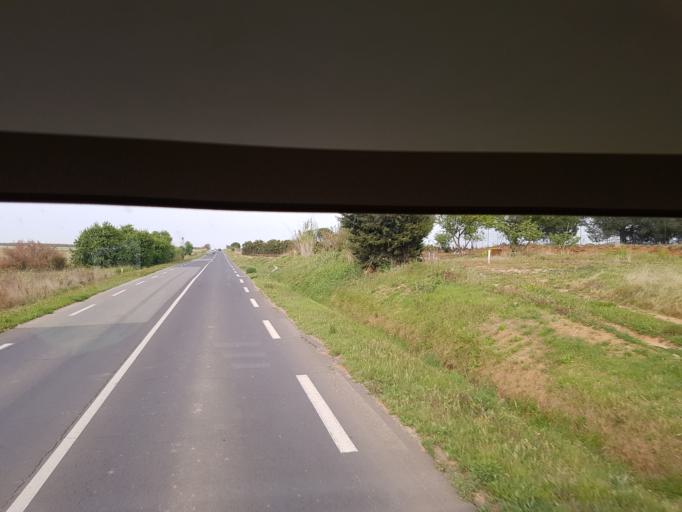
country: FR
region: Languedoc-Roussillon
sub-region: Departement de l'Herault
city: Marseillan
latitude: 43.3464
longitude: 3.5067
